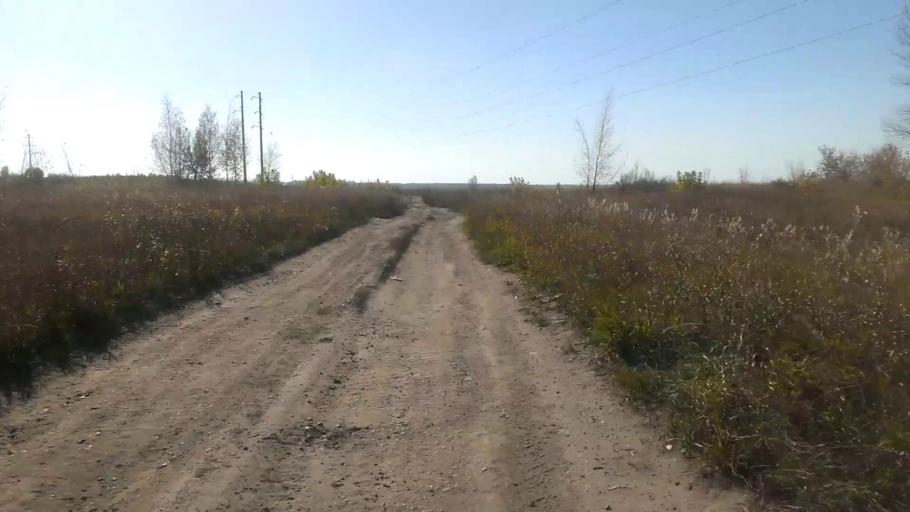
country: RU
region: Altai Krai
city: Novoaltaysk
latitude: 53.3672
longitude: 83.9461
